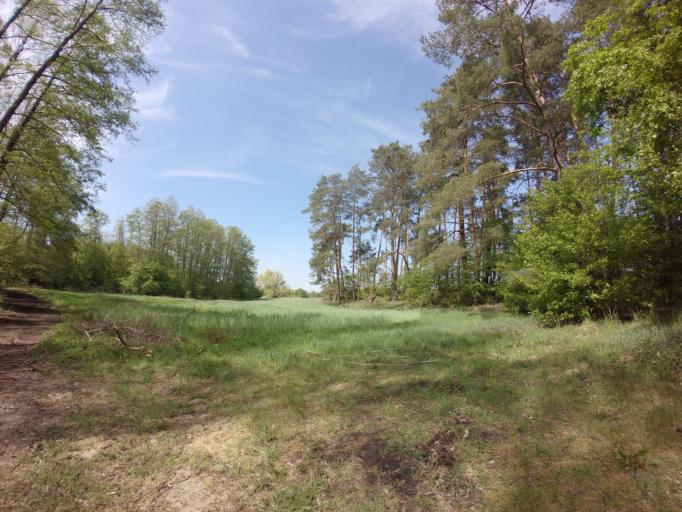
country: PL
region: West Pomeranian Voivodeship
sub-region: Powiat choszczenski
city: Choszczno
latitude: 53.2142
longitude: 15.4200
